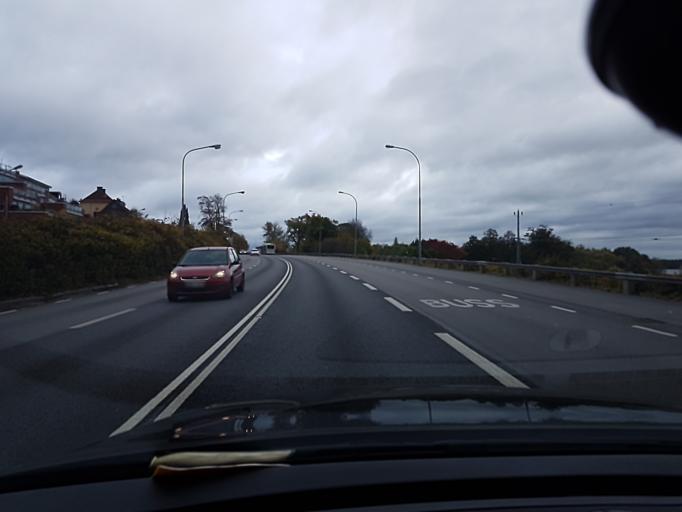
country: SE
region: Kronoberg
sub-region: Vaxjo Kommun
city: Vaexjoe
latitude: 56.8756
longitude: 14.8156
